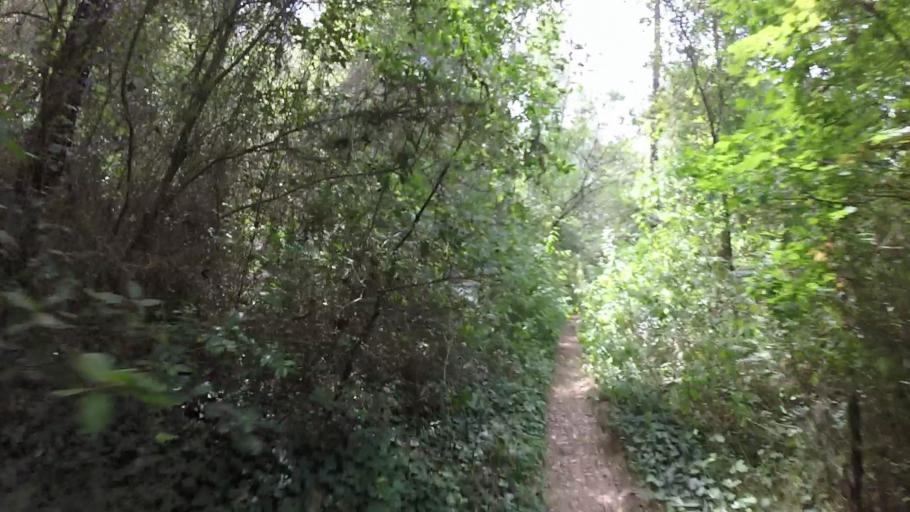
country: FR
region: Provence-Alpes-Cote d'Azur
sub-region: Departement des Alpes-Maritimes
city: Mougins
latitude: 43.6143
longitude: 7.0208
